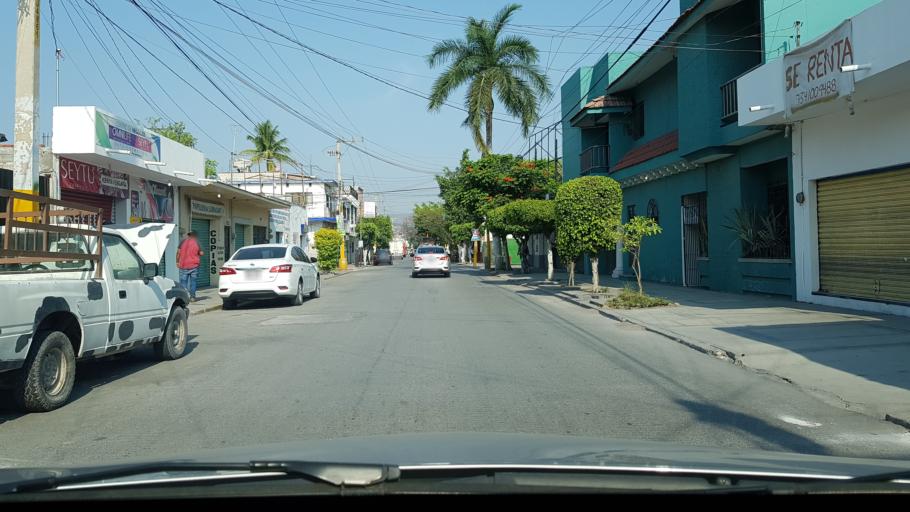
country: MX
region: Morelos
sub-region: Jojutla
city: Jojutla
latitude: 18.6179
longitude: -99.1778
